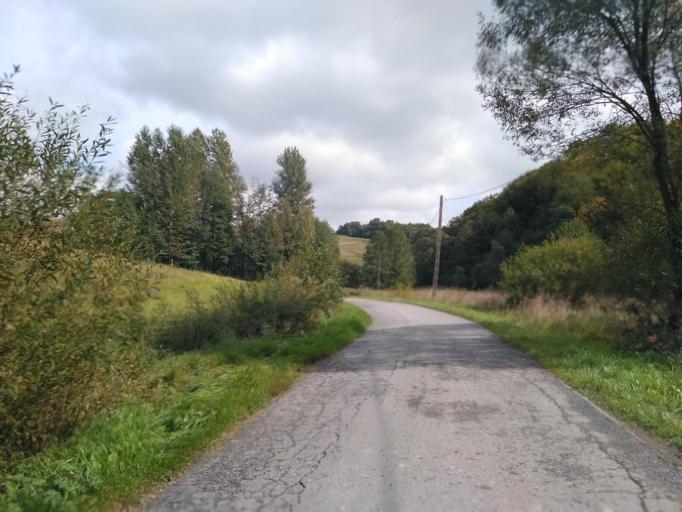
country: PL
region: Subcarpathian Voivodeship
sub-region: Powiat ropczycko-sedziszowski
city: Niedzwiada
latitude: 49.9395
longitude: 21.5231
